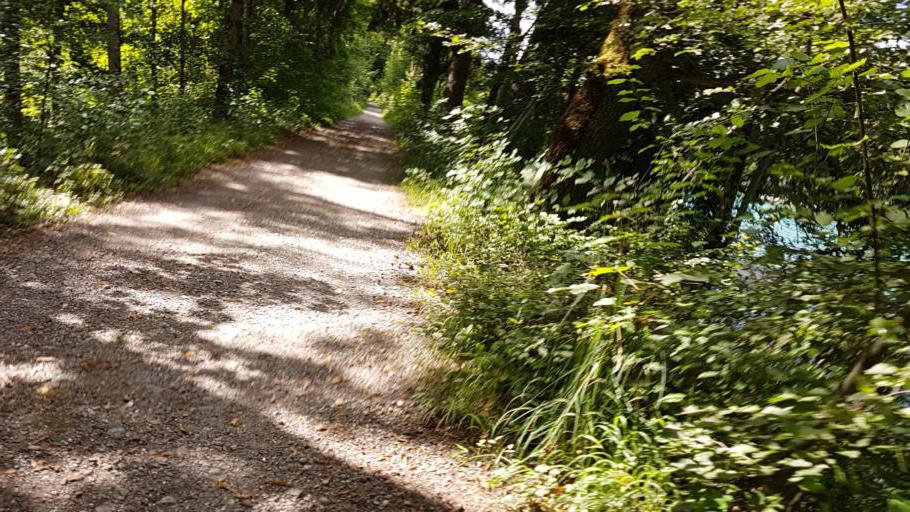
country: CH
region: Bern
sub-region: Bern-Mittelland District
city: Belp
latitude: 46.9081
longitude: 7.5143
